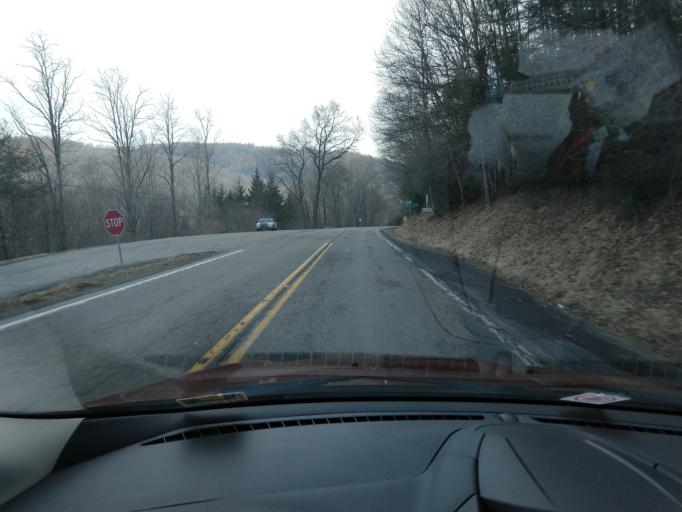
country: US
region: Virginia
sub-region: Highland County
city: Monterey
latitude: 38.4604
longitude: -79.5265
